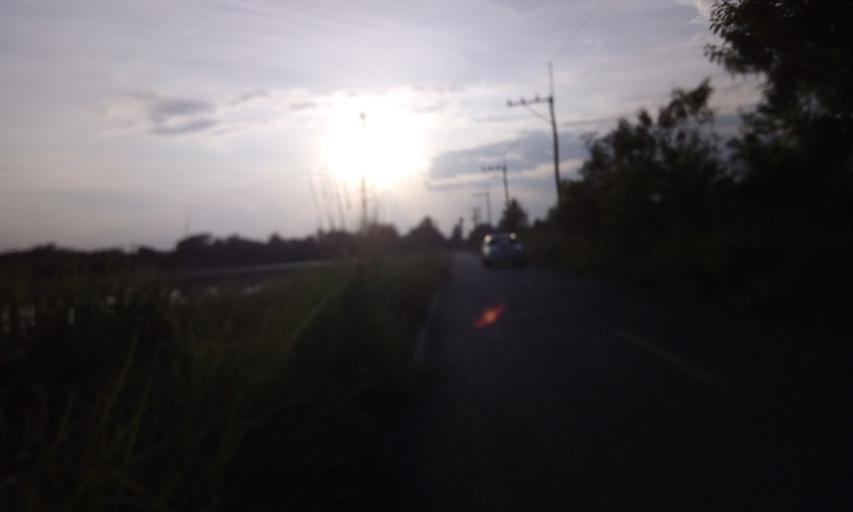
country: TH
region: Pathum Thani
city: Ban Rangsit
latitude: 14.0409
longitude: 100.8500
